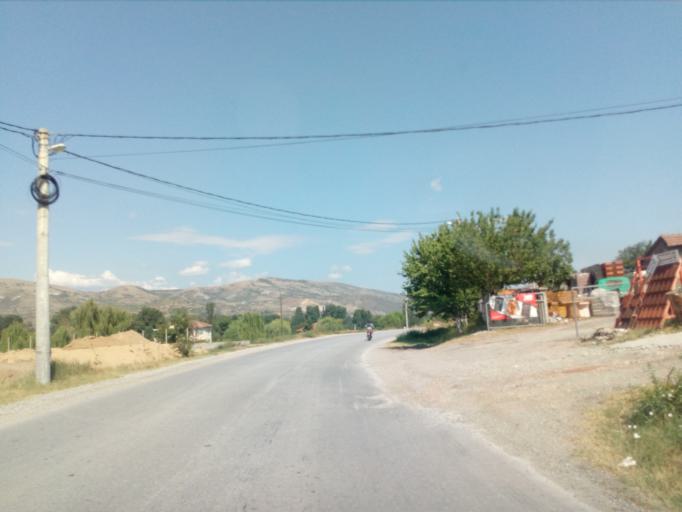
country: MK
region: Veles
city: Veles
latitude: 41.7281
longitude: 21.7795
